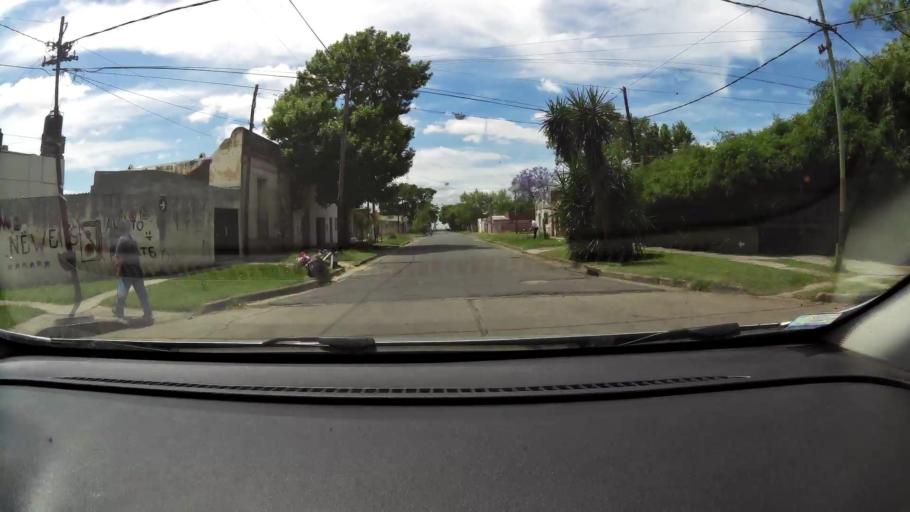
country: AR
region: Santa Fe
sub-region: Departamento de Rosario
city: Rosario
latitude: -32.9752
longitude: -60.6279
